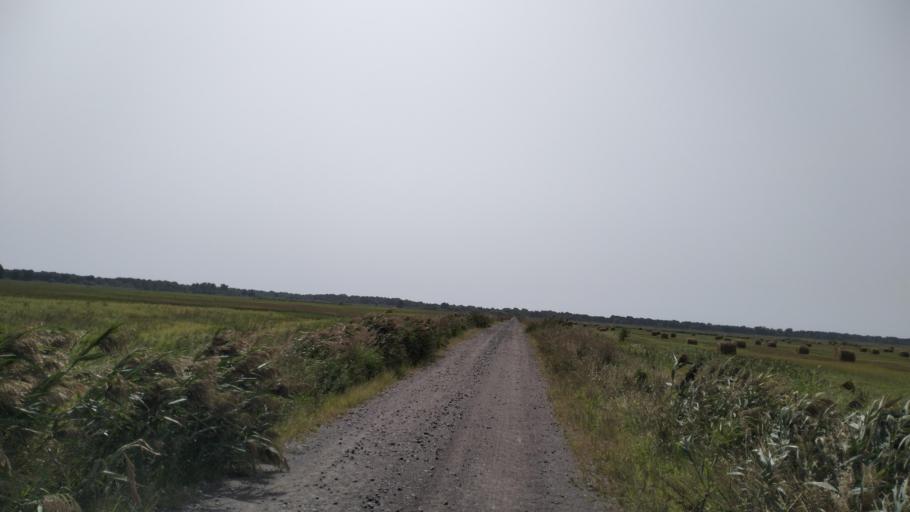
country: BY
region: Brest
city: Davyd-Haradok
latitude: 51.9805
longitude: 27.1748
